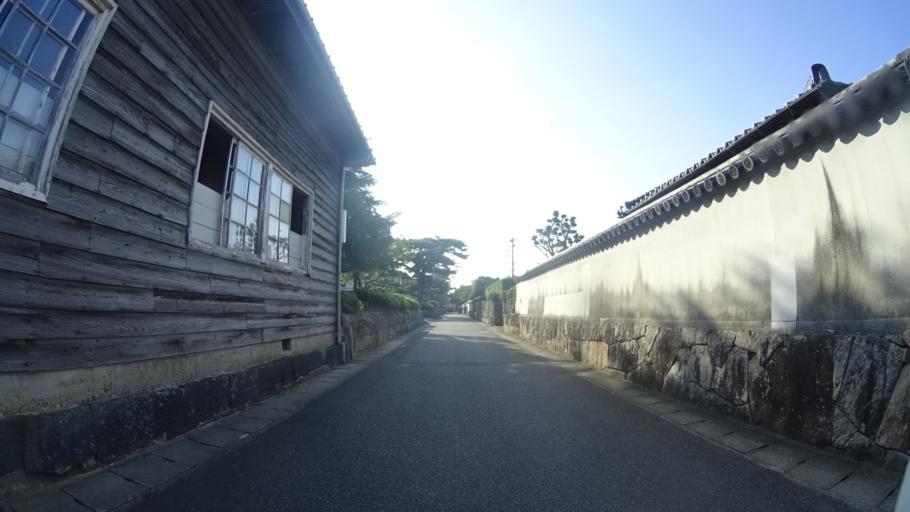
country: JP
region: Yamaguchi
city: Hagi
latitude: 34.4132
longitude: 131.3869
